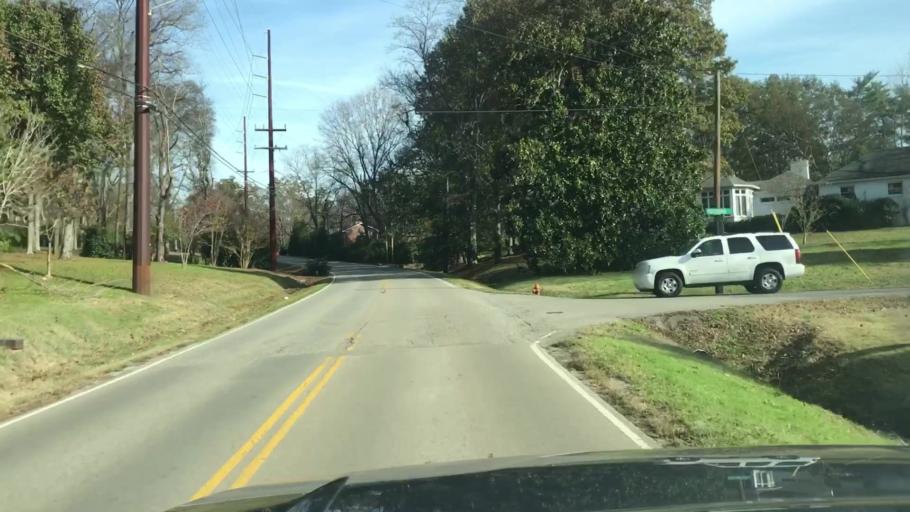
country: US
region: Tennessee
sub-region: Davidson County
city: Belle Meade
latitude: 36.1168
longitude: -86.8803
